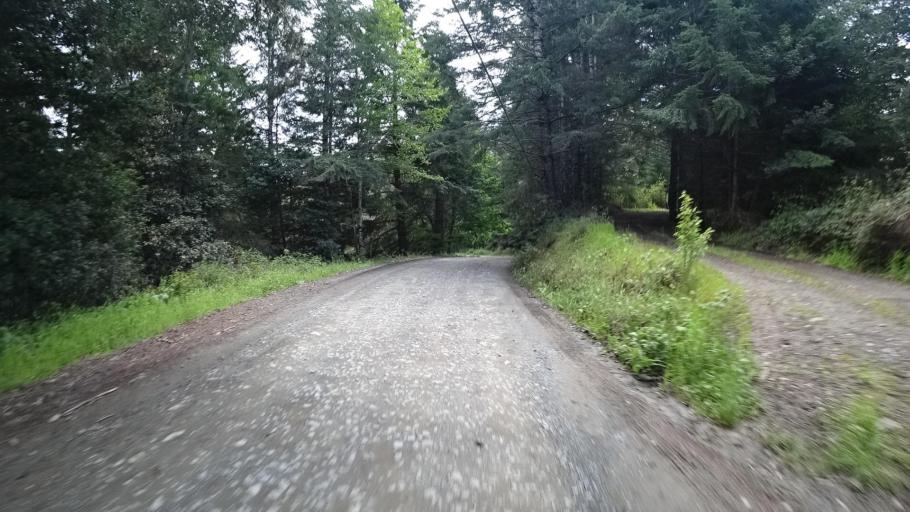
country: US
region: California
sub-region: Humboldt County
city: Blue Lake
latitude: 40.7860
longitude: -123.8807
